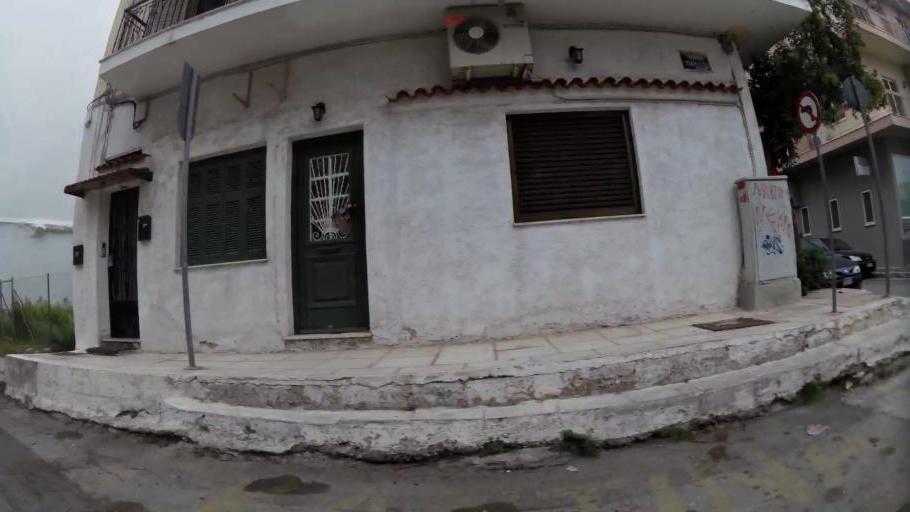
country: GR
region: Attica
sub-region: Nomarchia Athinas
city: Ilion
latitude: 38.0295
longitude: 23.7090
